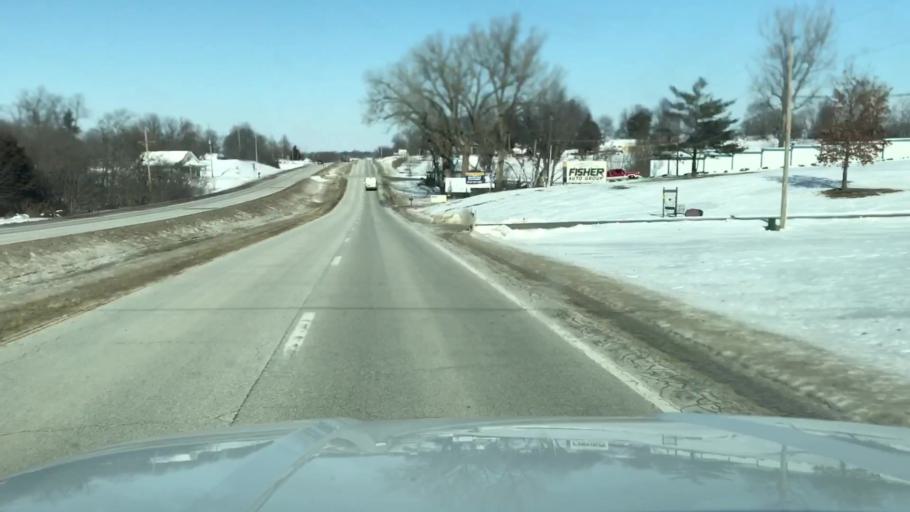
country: US
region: Missouri
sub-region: Andrew County
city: Savannah
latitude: 39.9140
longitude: -94.8107
